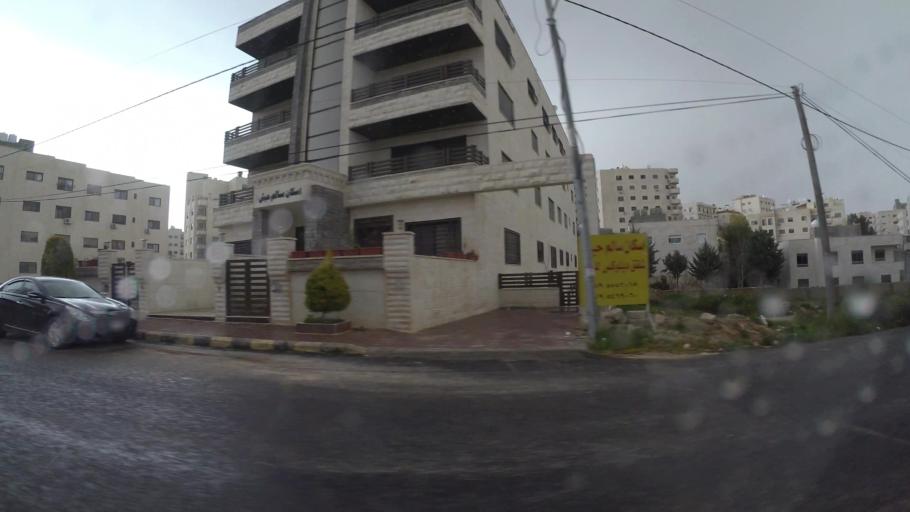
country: JO
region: Amman
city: Umm as Summaq
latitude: 31.8804
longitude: 35.8546
